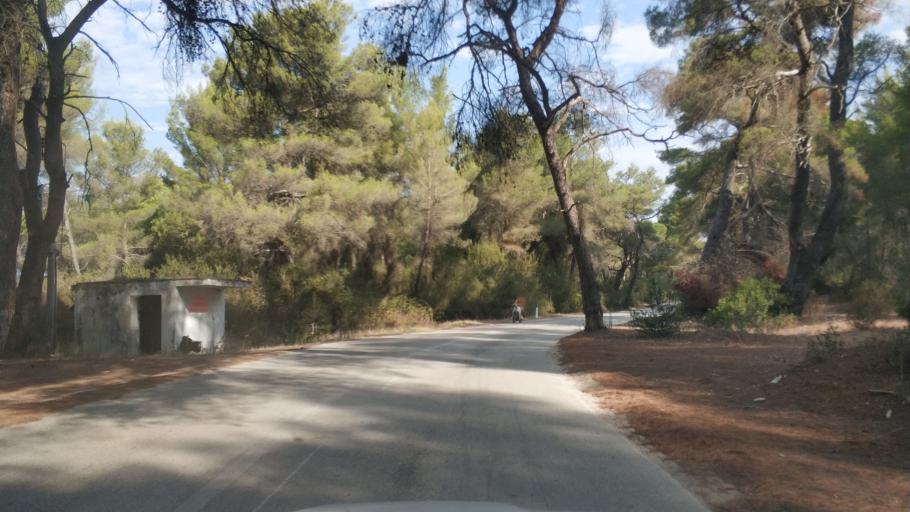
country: AL
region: Fier
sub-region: Rrethi i Lushnjes
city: Divjake
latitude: 40.9825
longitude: 19.4826
